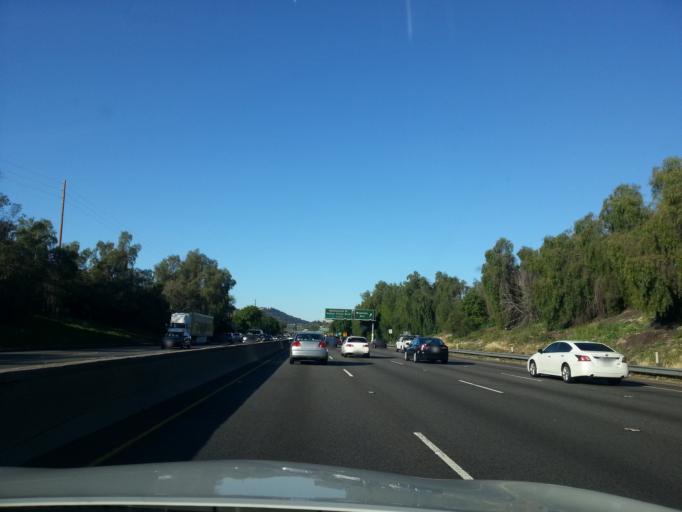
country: US
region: California
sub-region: Los Angeles County
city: Calabasas
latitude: 34.1632
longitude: -118.6272
